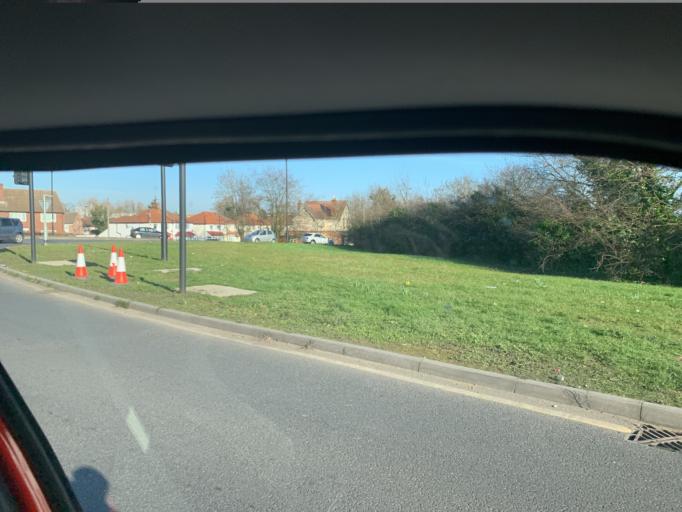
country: GB
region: England
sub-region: Slough
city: Slough
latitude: 51.5084
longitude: -0.6123
